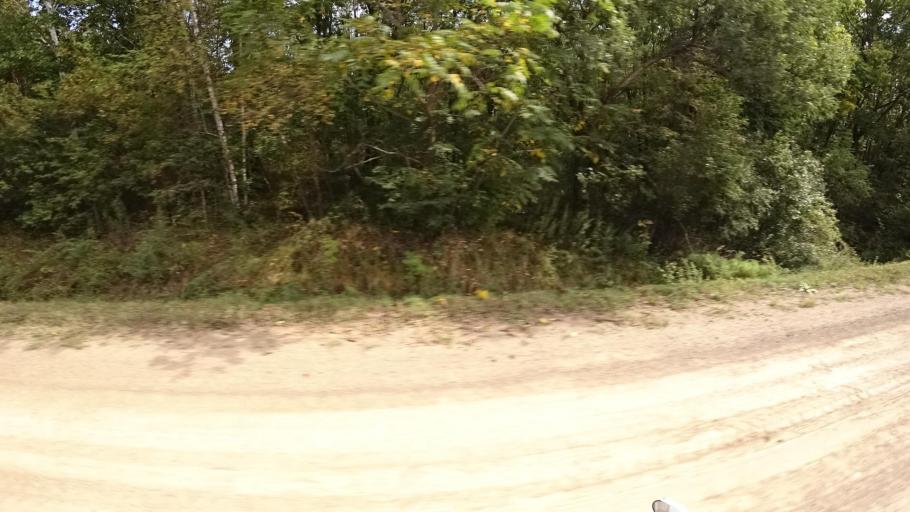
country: RU
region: Primorskiy
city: Yakovlevka
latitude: 44.7411
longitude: 133.6070
